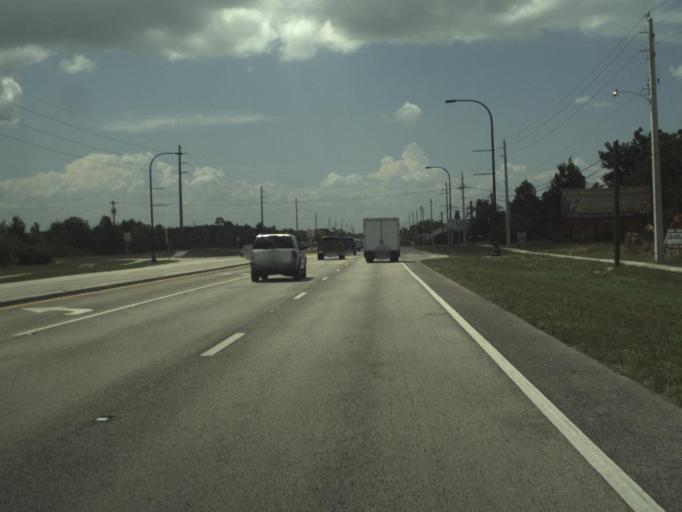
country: US
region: Florida
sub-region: Martin County
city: Hobe Sound
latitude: 27.0861
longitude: -80.1493
